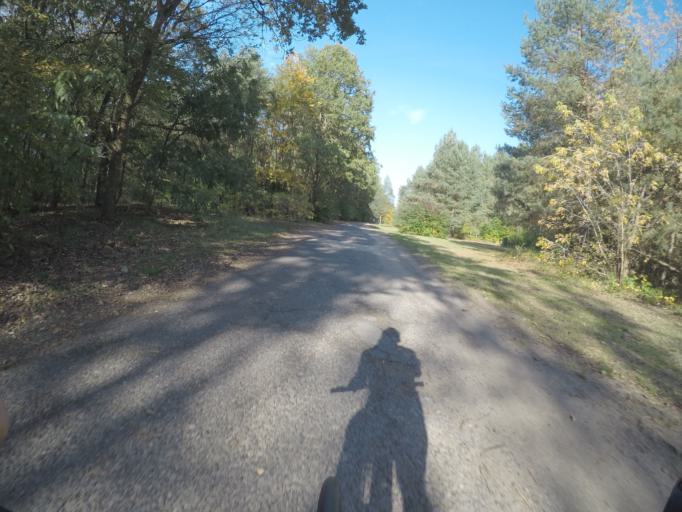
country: DE
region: Brandenburg
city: Hohen Neuendorf
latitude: 52.6701
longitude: 13.2402
